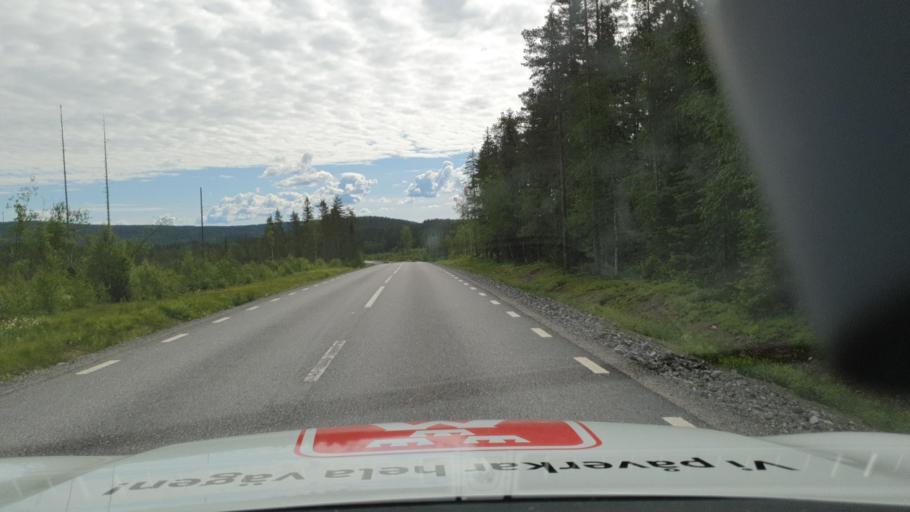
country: SE
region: Vaesterbotten
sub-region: Umea Kommun
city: Ersmark
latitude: 64.2582
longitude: 20.1965
